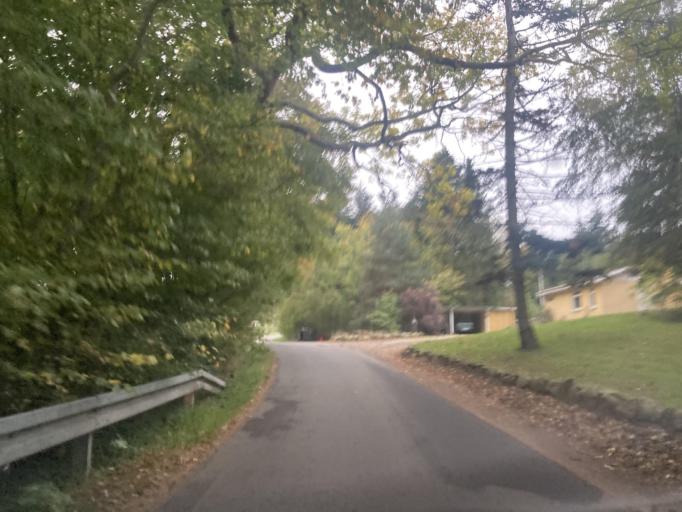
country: DK
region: Capital Region
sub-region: Egedal Kommune
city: Vekso
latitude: 55.7268
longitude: 12.2143
